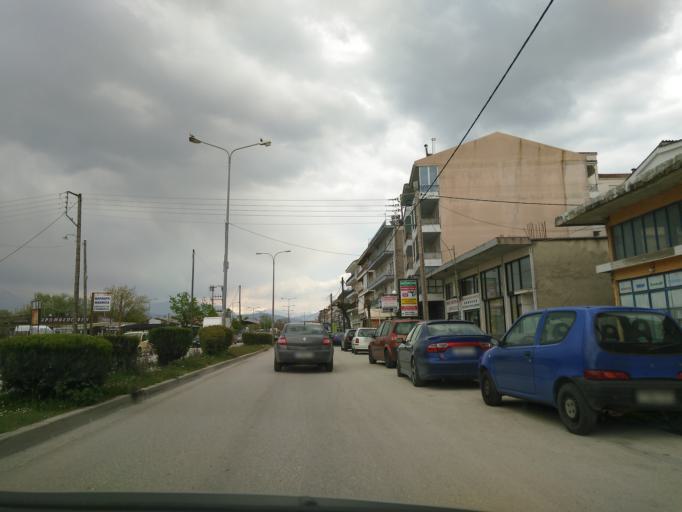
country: GR
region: Epirus
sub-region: Nomos Ioanninon
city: Ioannina
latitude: 39.6754
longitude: 20.8447
